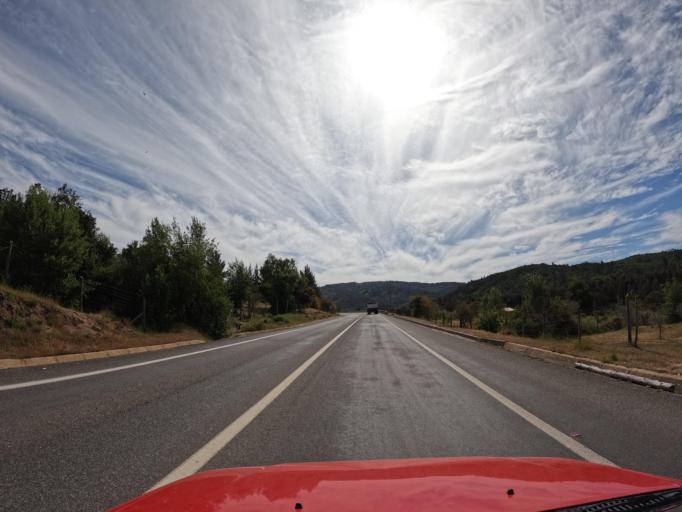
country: CL
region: Maule
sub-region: Provincia de Talca
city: Talca
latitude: -35.1712
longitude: -71.9745
